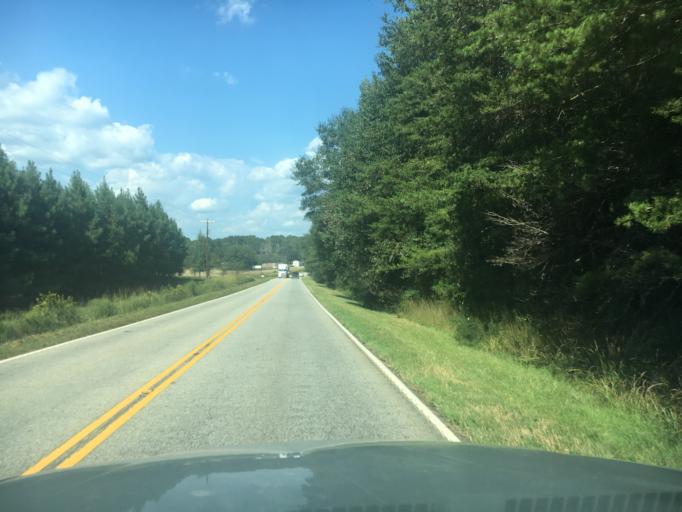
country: US
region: South Carolina
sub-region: Anderson County
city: Pendleton
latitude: 34.6072
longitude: -82.7904
